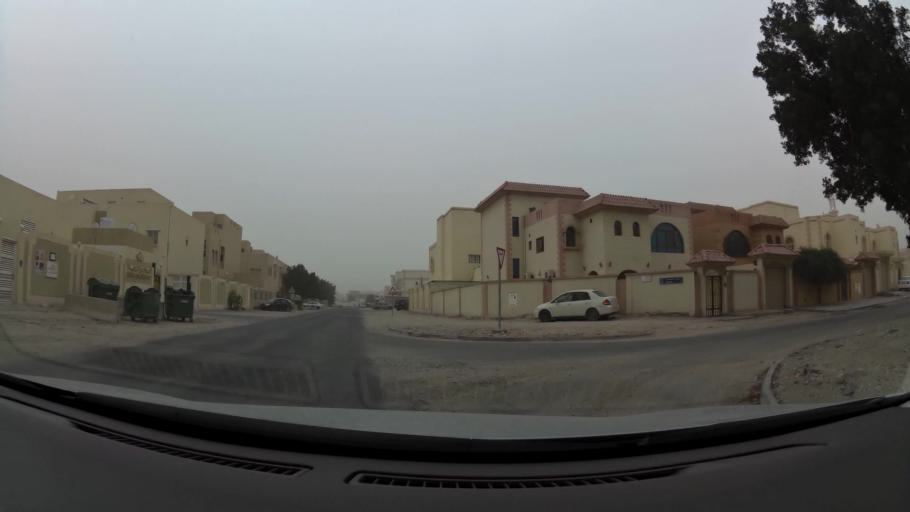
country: QA
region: Baladiyat ad Dawhah
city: Doha
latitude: 25.2487
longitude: 51.4870
